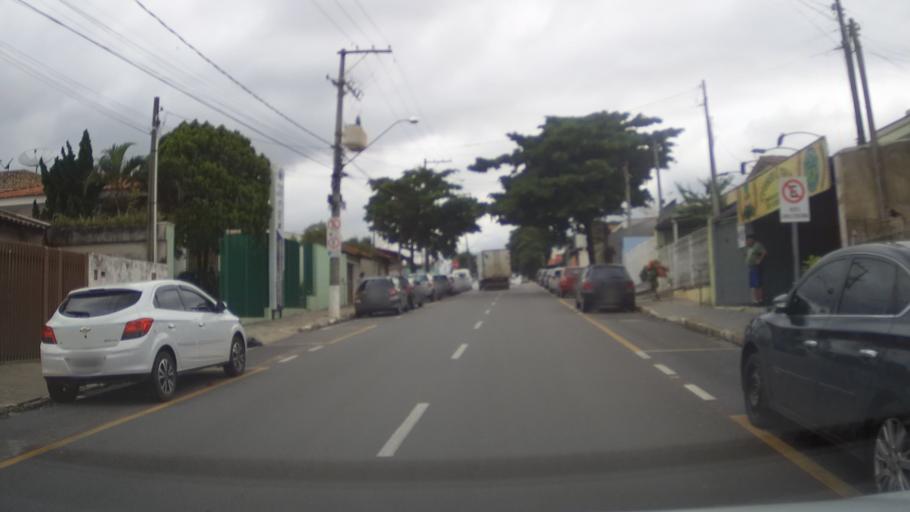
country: BR
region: Sao Paulo
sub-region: Louveira
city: Louveira
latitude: -23.0870
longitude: -46.9767
